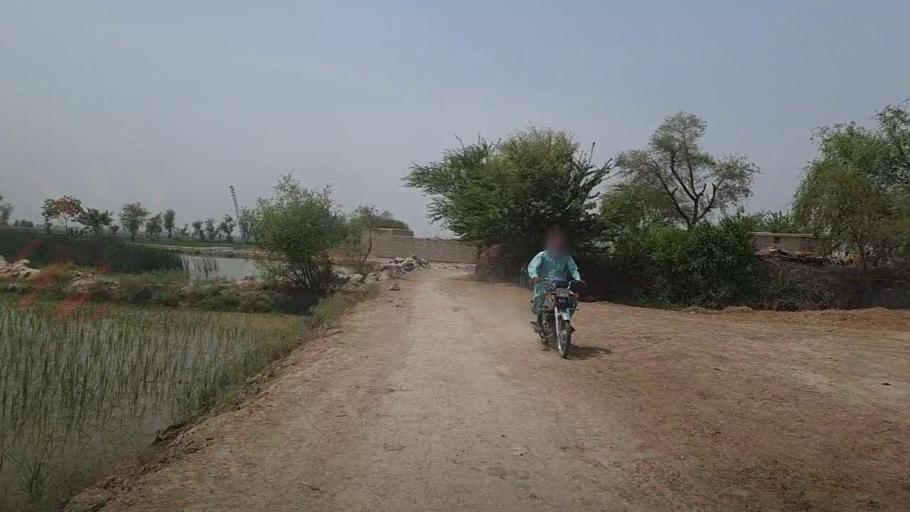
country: PK
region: Sindh
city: Sita Road
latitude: 27.0946
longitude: 67.8545
